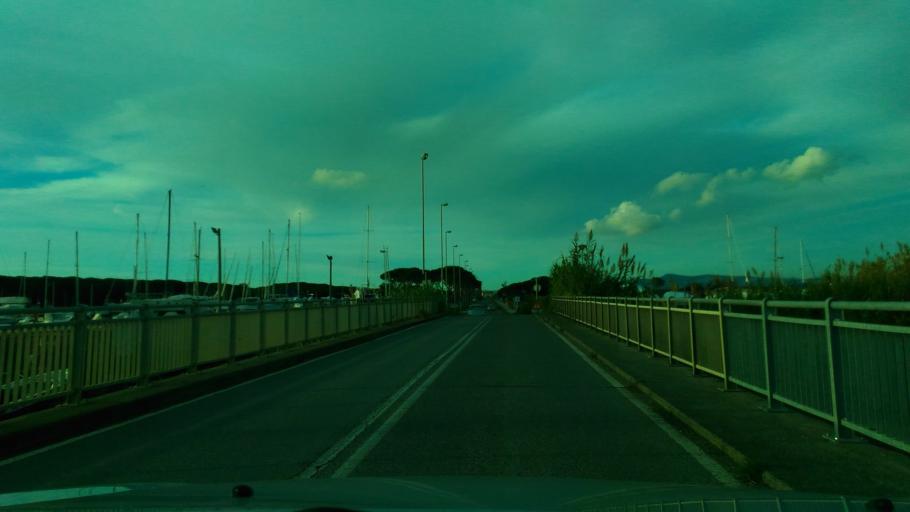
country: IT
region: Tuscany
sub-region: Provincia di Livorno
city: Cecina
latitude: 43.3042
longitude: 10.4931
